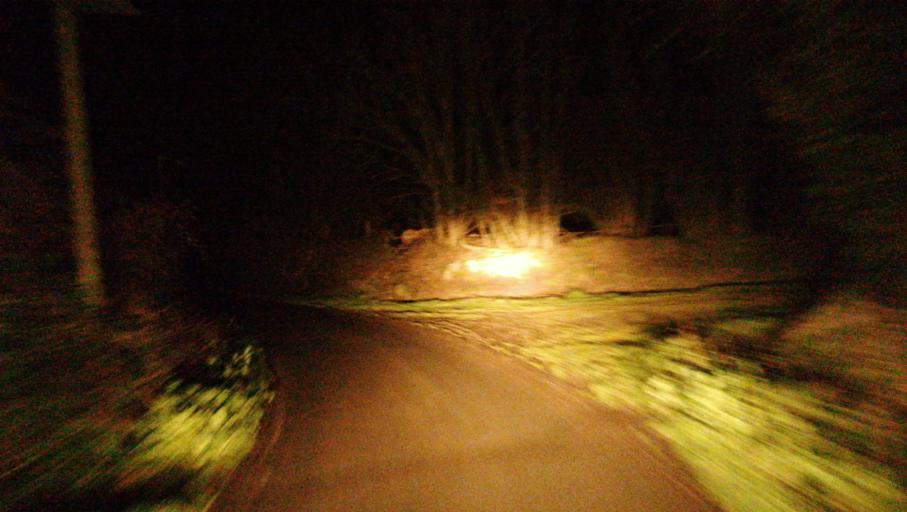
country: FR
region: Brittany
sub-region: Departement des Cotes-d'Armor
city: Plehedel
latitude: 48.6608
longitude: -3.0117
